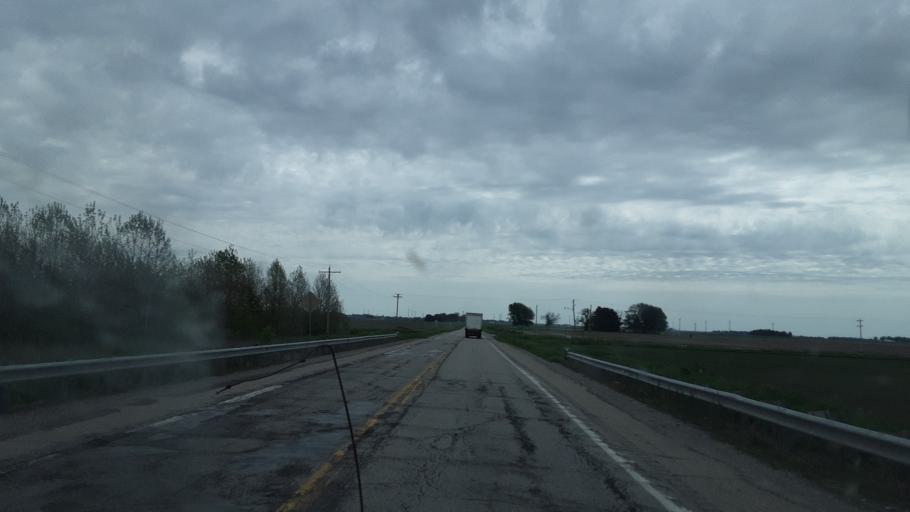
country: US
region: Illinois
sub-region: Tazewell County
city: Delavan
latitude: 40.3074
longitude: -89.4913
